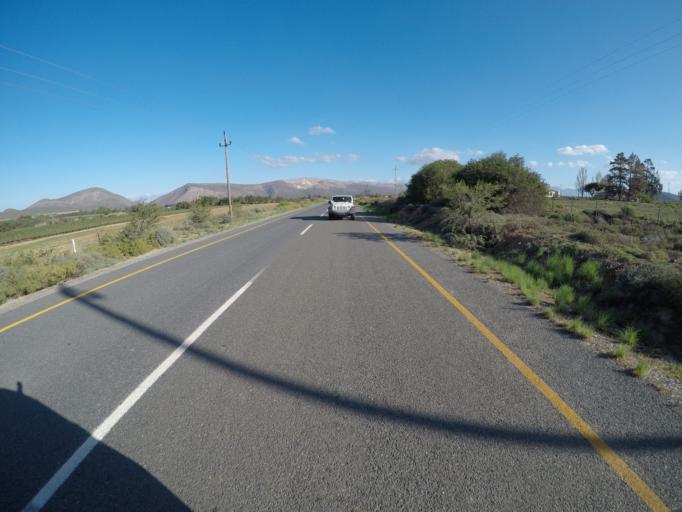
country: ZA
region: Western Cape
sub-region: Cape Winelands District Municipality
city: Ashton
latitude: -33.7985
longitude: 19.7811
